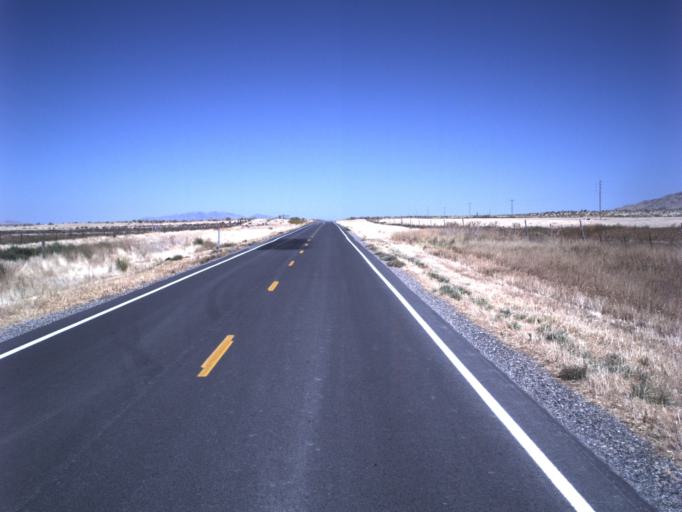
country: US
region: Utah
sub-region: Tooele County
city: Grantsville
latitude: 40.5039
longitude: -112.7480
